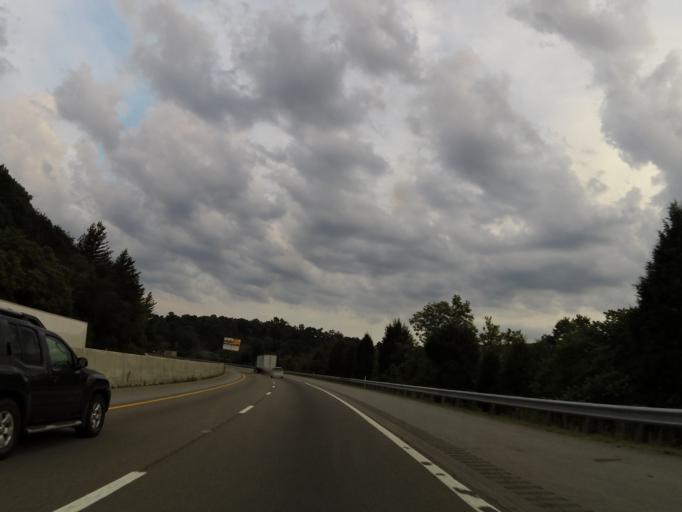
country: US
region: Tennessee
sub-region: Anderson County
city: Norris
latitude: 36.1199
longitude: -84.0343
